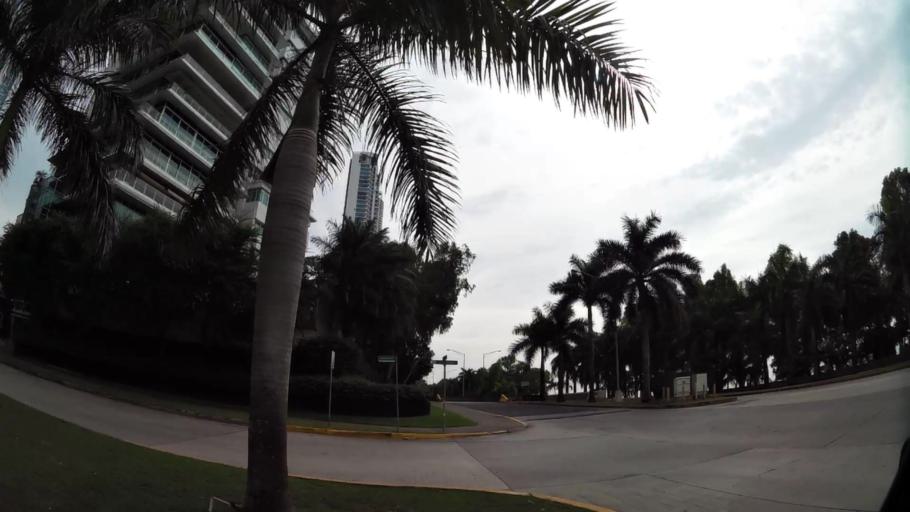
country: PA
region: Panama
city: San Miguelito
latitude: 9.0099
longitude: -79.4701
